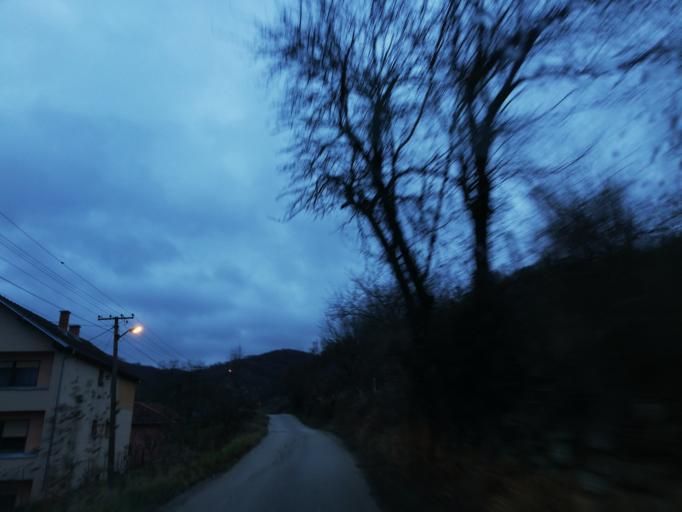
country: RS
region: Central Serbia
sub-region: Pirotski Okrug
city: Dimitrovgrad
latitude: 43.0099
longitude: 22.7196
